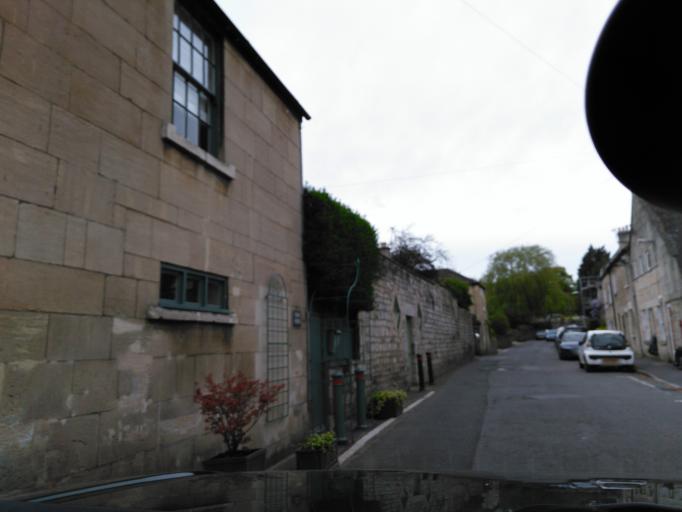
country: GB
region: England
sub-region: Bath and North East Somerset
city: Bath
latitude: 51.3962
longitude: -2.3221
